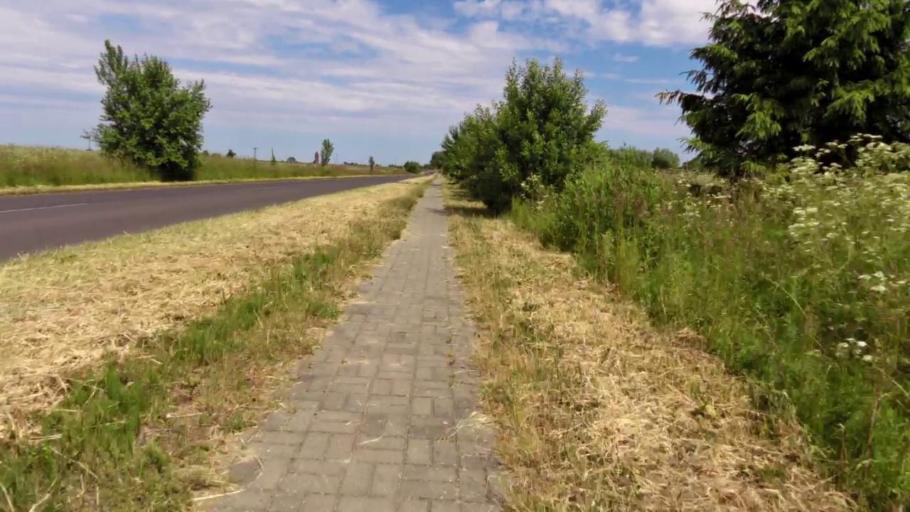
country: PL
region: West Pomeranian Voivodeship
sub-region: Powiat kamienski
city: Kamien Pomorski
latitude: 53.9552
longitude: 14.6830
